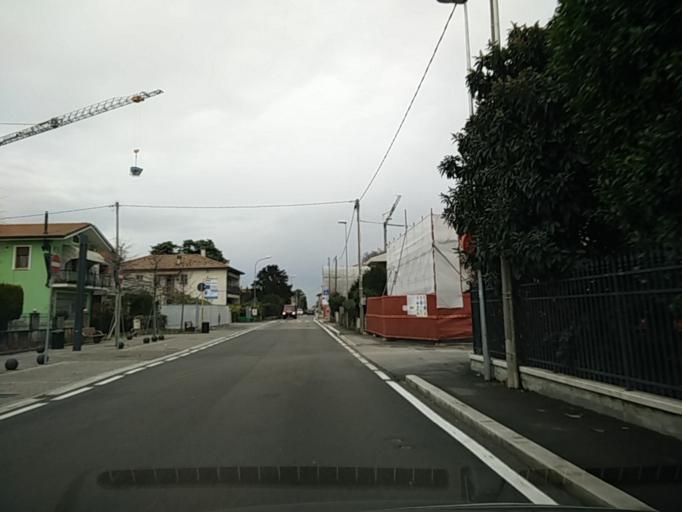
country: IT
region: Veneto
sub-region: Provincia di Treviso
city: Caselle
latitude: 45.7437
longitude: 11.9799
